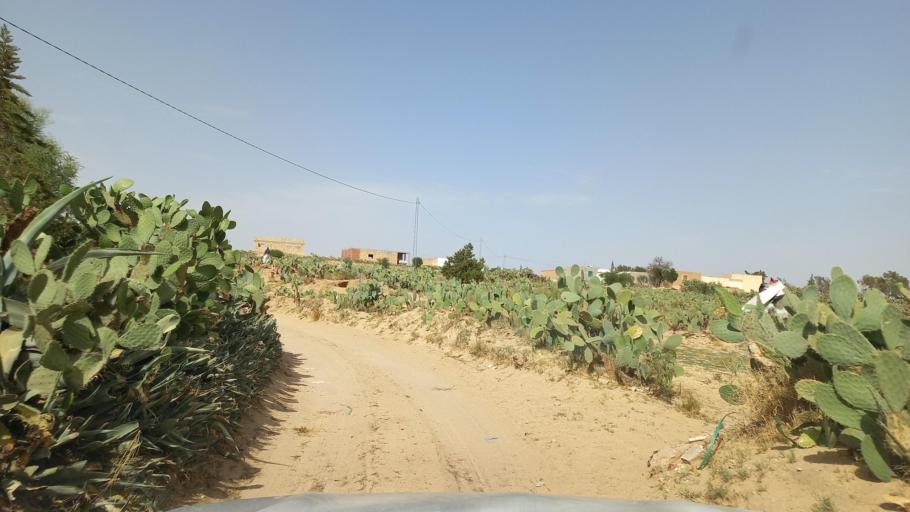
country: TN
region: Al Qasrayn
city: Kasserine
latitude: 35.2976
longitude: 8.9483
